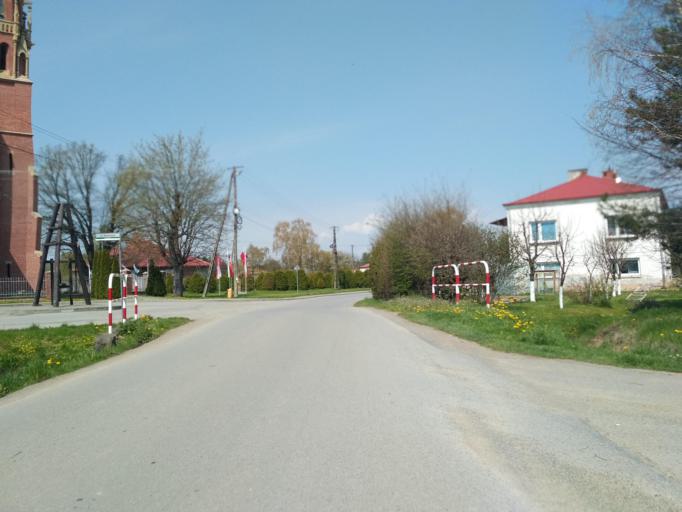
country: PL
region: Subcarpathian Voivodeship
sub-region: Powiat krosnienski
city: Chorkowka
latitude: 49.6286
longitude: 21.7028
